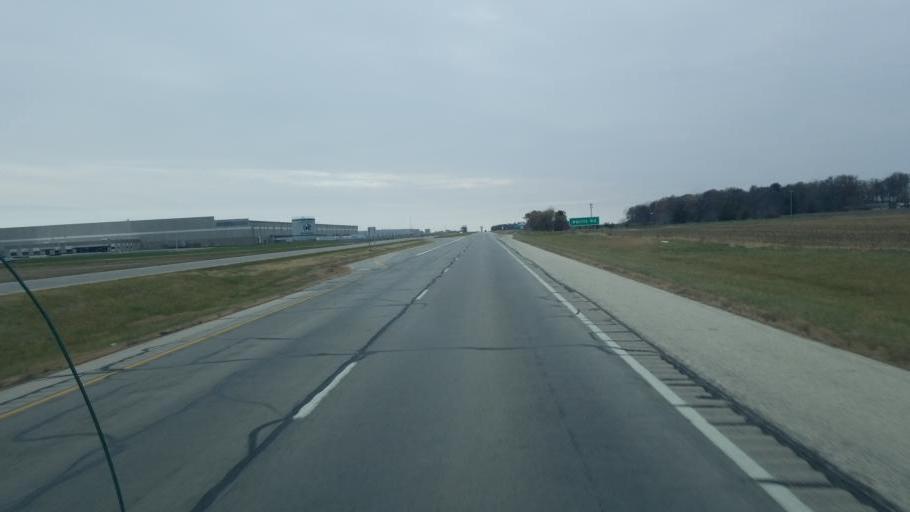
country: US
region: Ohio
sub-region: Auglaize County
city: Saint Marys
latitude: 40.5574
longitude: -84.4624
